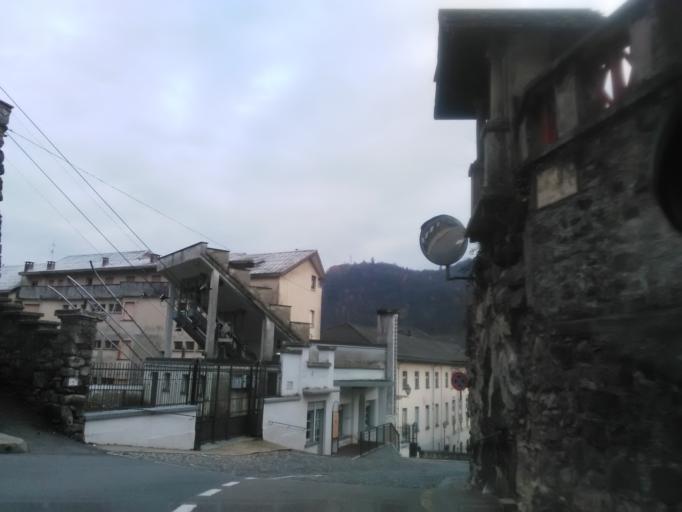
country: IT
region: Piedmont
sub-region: Provincia di Vercelli
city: Varallo
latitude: 45.8181
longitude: 8.2532
